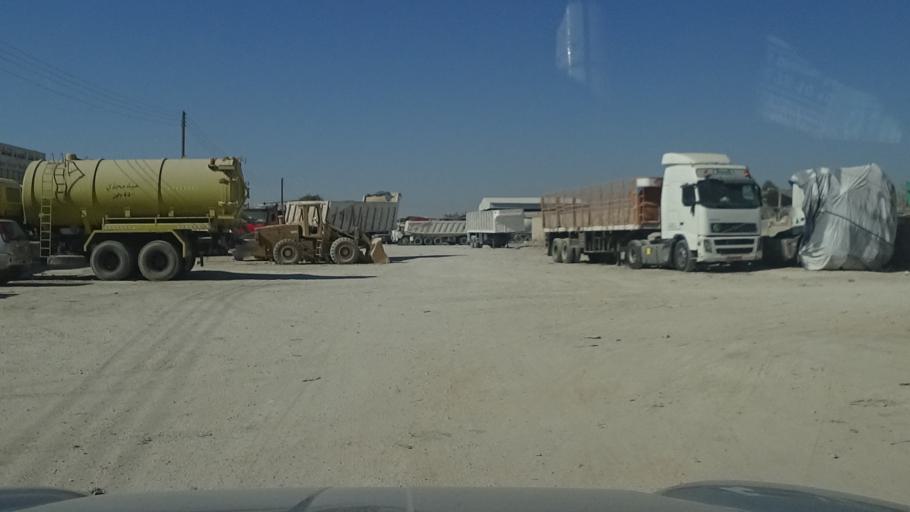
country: OM
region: Zufar
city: Salalah
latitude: 17.0293
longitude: 54.0433
